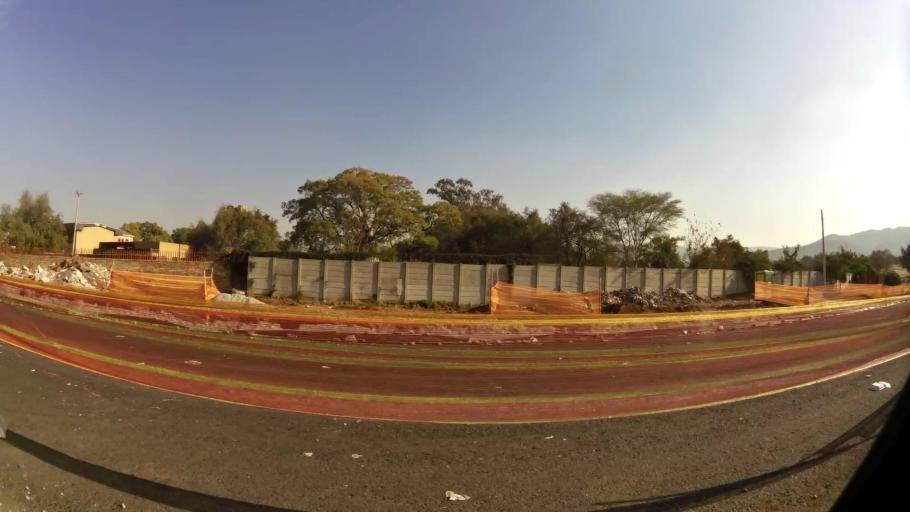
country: ZA
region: North-West
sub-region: Bojanala Platinum District Municipality
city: Rustenburg
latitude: -25.6634
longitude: 27.2342
